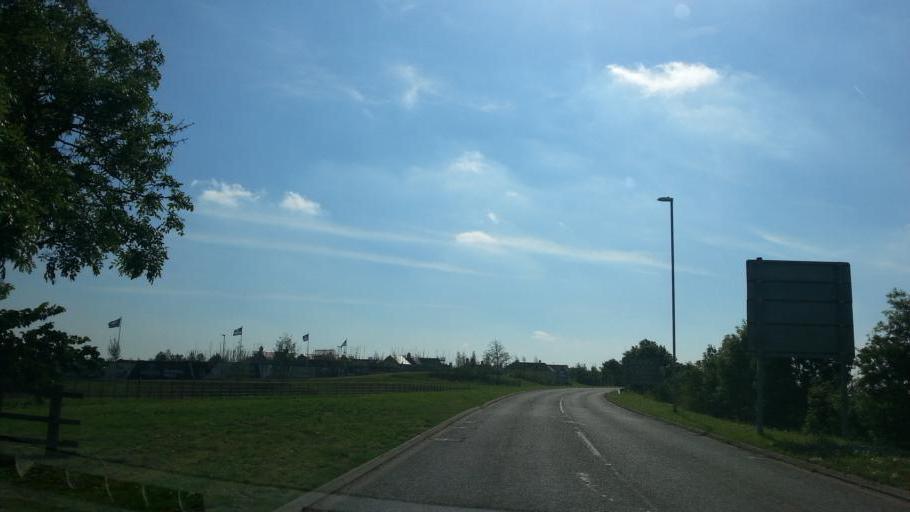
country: GB
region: England
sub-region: Cambridgeshire
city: Great Stukeley
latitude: 52.3711
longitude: -0.2398
